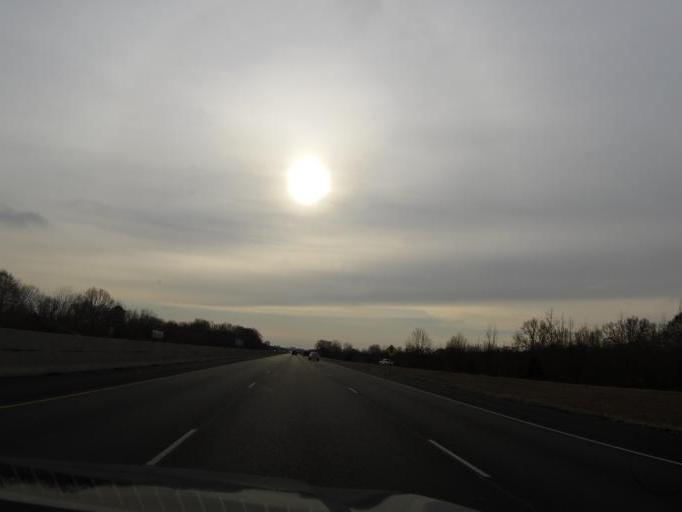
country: US
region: Alabama
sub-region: Elmore County
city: Millbrook
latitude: 32.4161
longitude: -86.3550
